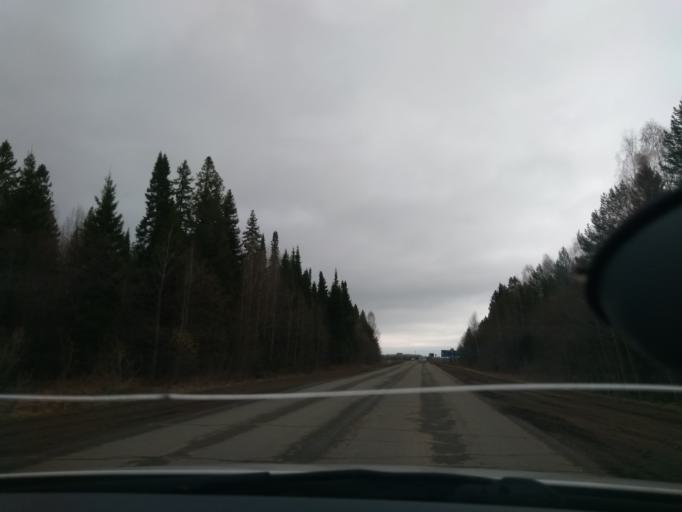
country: RU
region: Perm
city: Kungur
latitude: 57.3979
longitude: 56.8788
